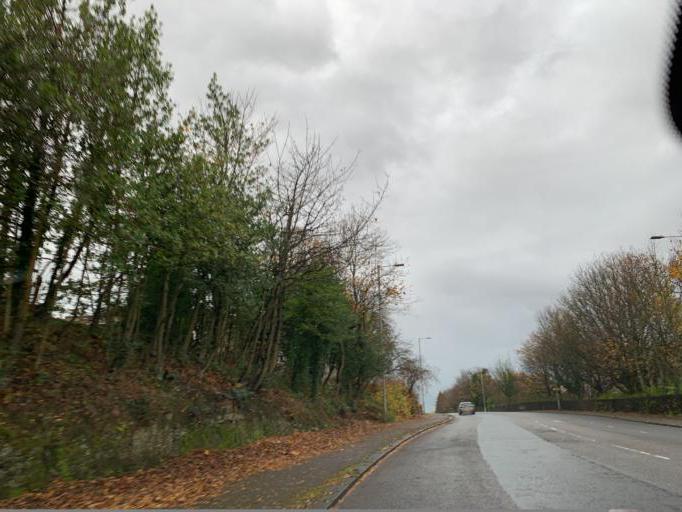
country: GB
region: Scotland
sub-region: East Renfrewshire
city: Giffnock
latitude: 55.8143
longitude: -4.2802
